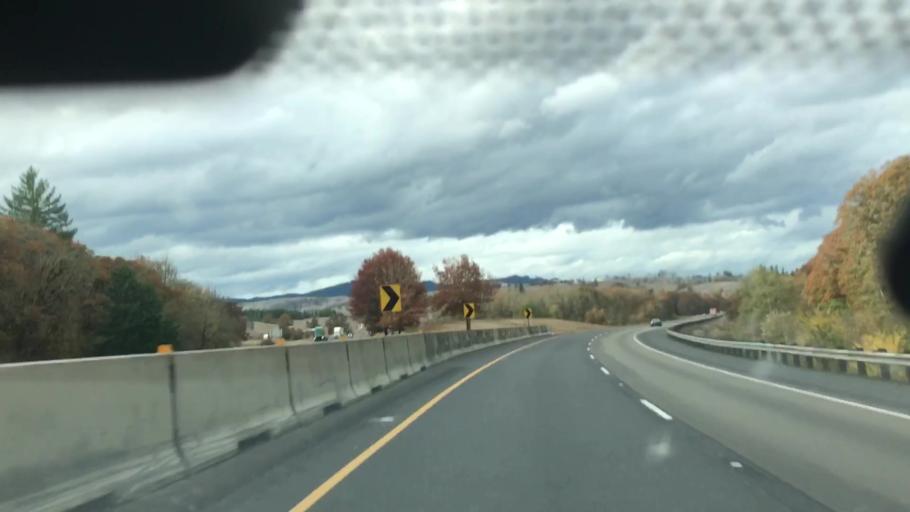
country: US
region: Oregon
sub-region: Douglas County
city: Sutherlin
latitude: 43.4466
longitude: -123.3225
